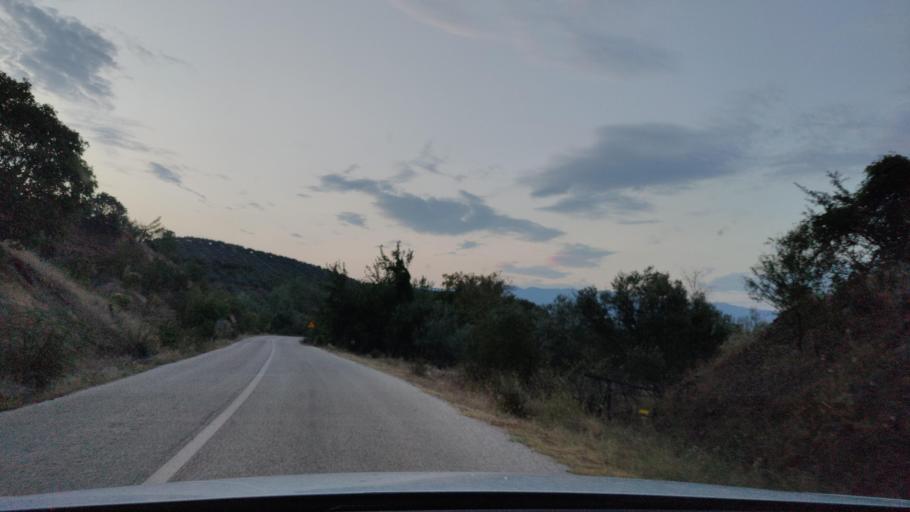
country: GR
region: Central Macedonia
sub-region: Nomos Serron
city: Chrysochorafa
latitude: 41.1431
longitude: 23.2134
